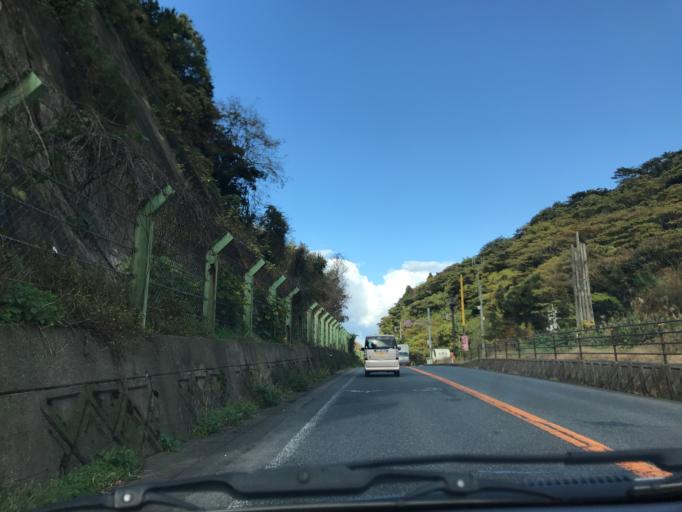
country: JP
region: Shimane
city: Yasugicho
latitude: 35.4229
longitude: 133.2862
